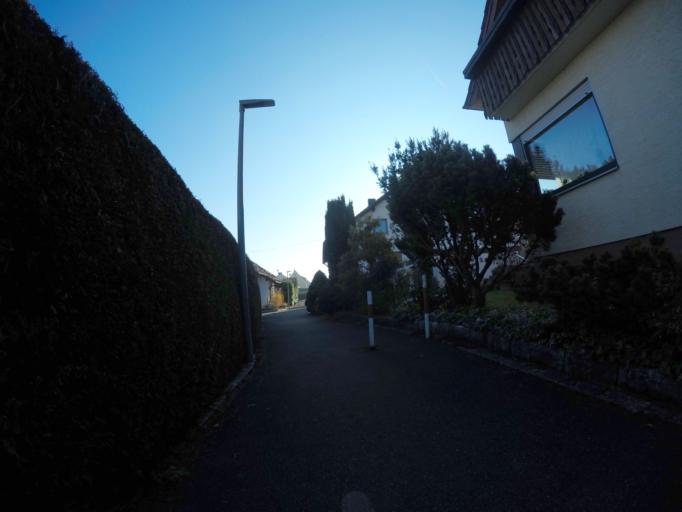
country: DE
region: Baden-Wuerttemberg
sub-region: Tuebingen Region
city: Pliezhausen
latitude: 48.5258
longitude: 9.2252
